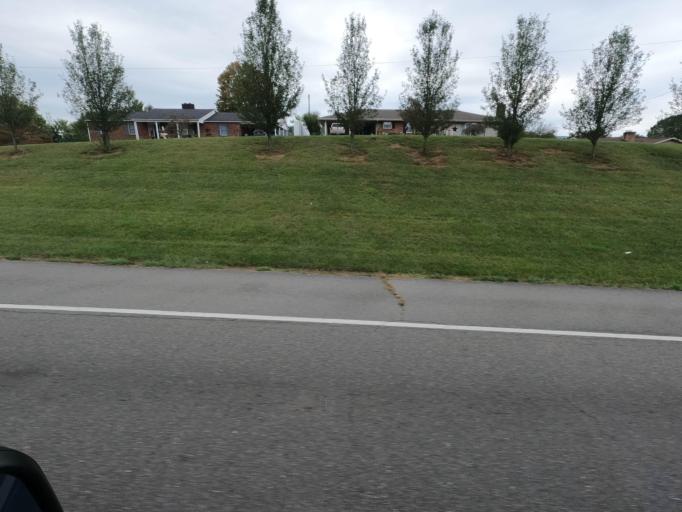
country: US
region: Tennessee
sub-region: Sullivan County
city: Kingsport
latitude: 36.5553
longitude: -82.6028
